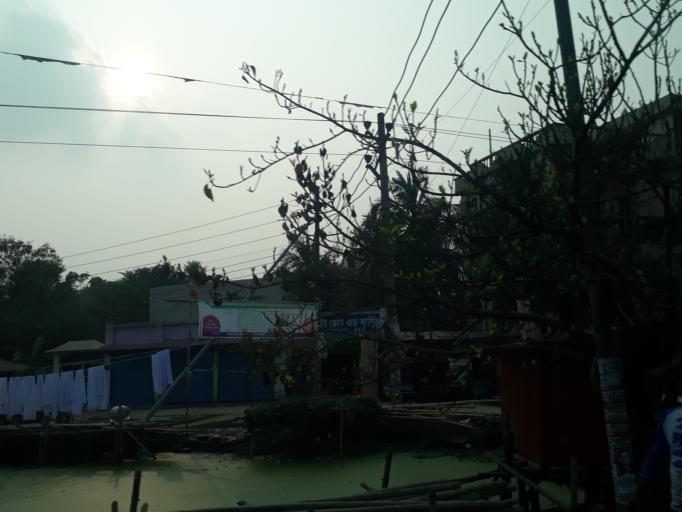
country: BD
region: Khulna
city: Khulna
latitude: 22.8957
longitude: 89.5105
